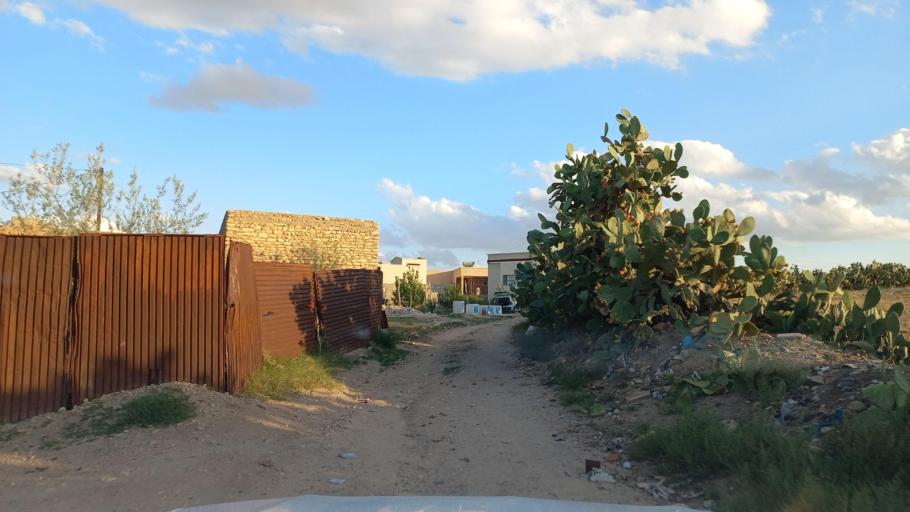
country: TN
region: Al Qasrayn
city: Sbiba
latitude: 35.3789
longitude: 9.0510
